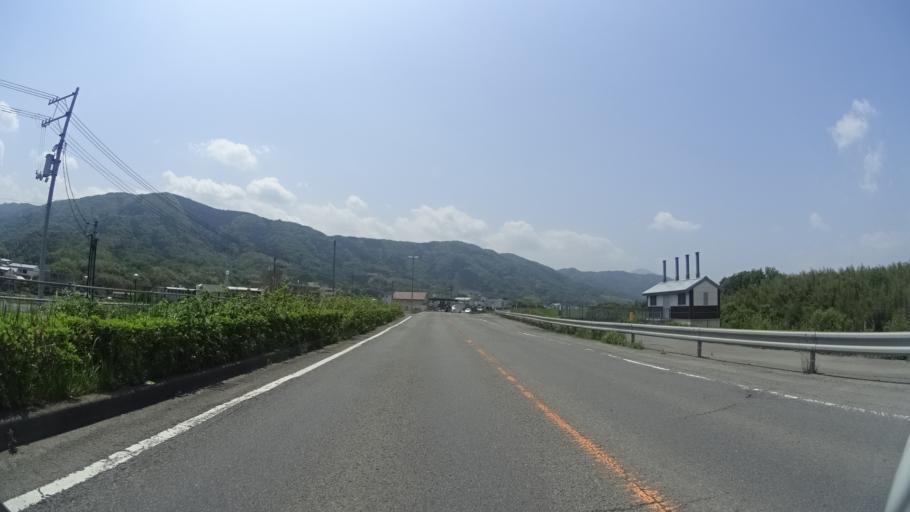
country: JP
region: Tokushima
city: Kamojimacho-jogejima
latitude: 34.0634
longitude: 134.3173
